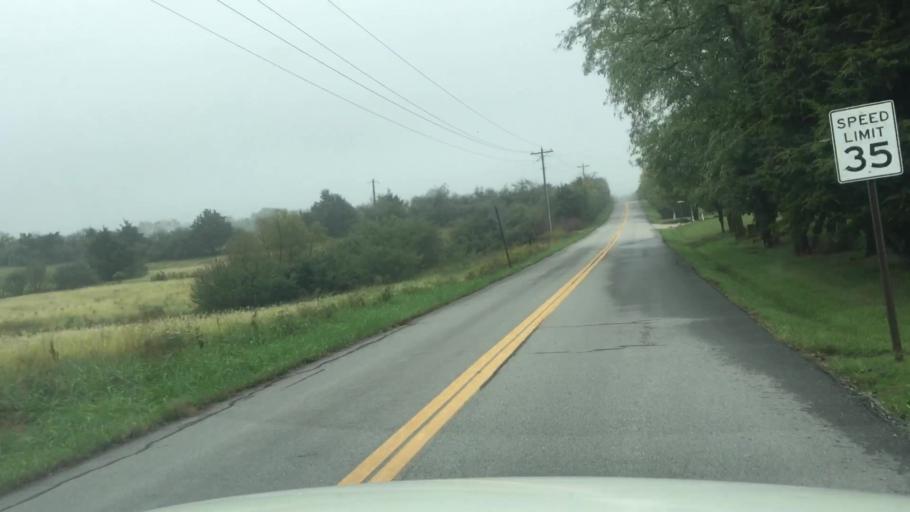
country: US
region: Missouri
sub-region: Boone County
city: Ashland
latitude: 38.8555
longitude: -92.3058
